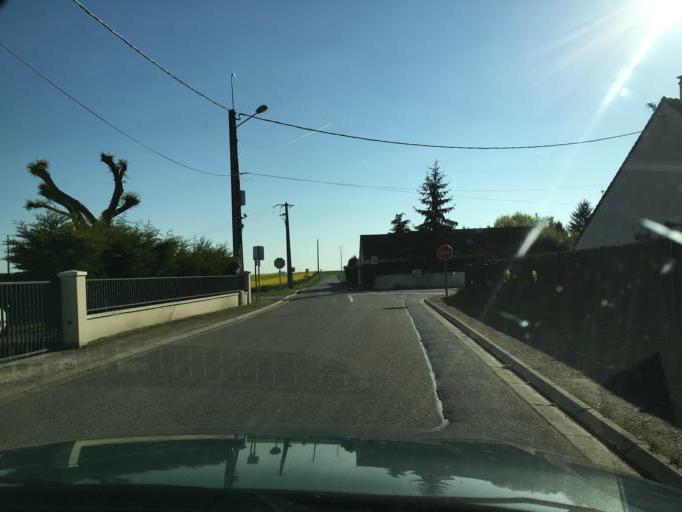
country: FR
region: Centre
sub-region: Departement du Loiret
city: Baule
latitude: 47.8354
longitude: 1.6568
